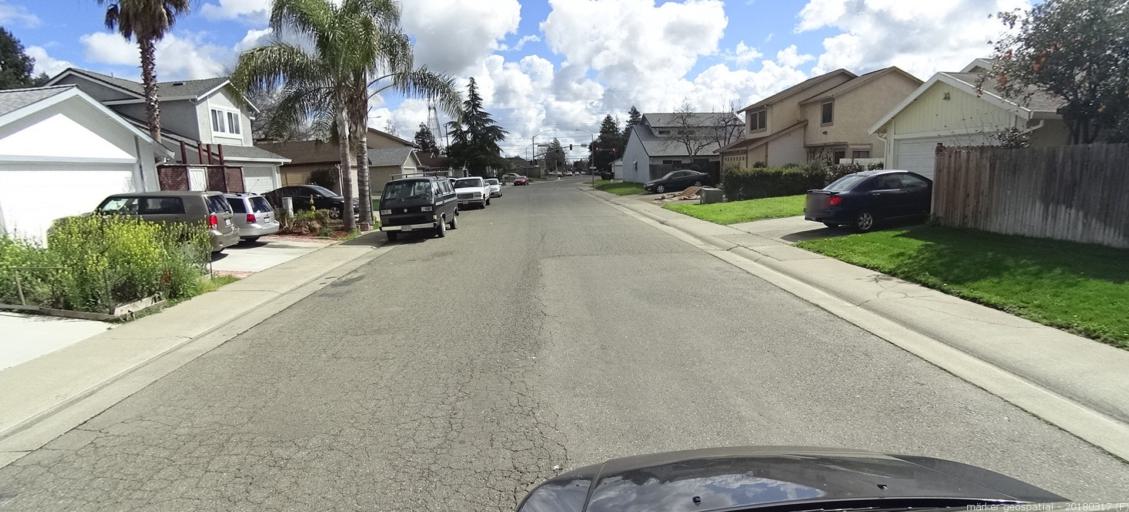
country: US
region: California
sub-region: Sacramento County
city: Florin
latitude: 38.4777
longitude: -121.4103
